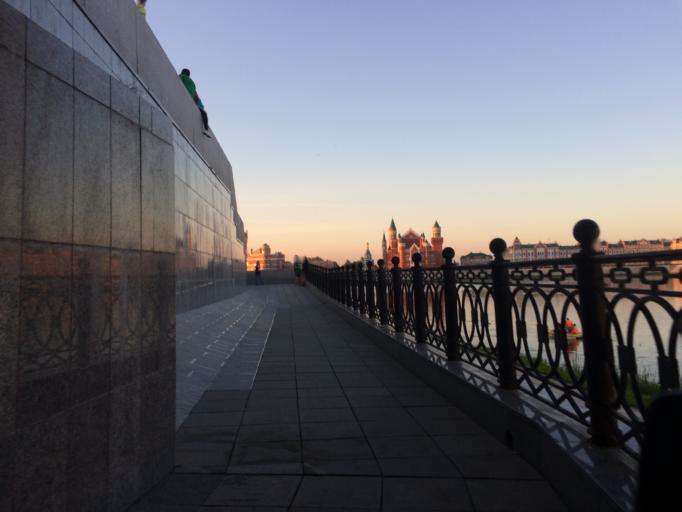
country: RU
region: Mariy-El
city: Yoshkar-Ola
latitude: 56.6333
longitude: 47.9056
